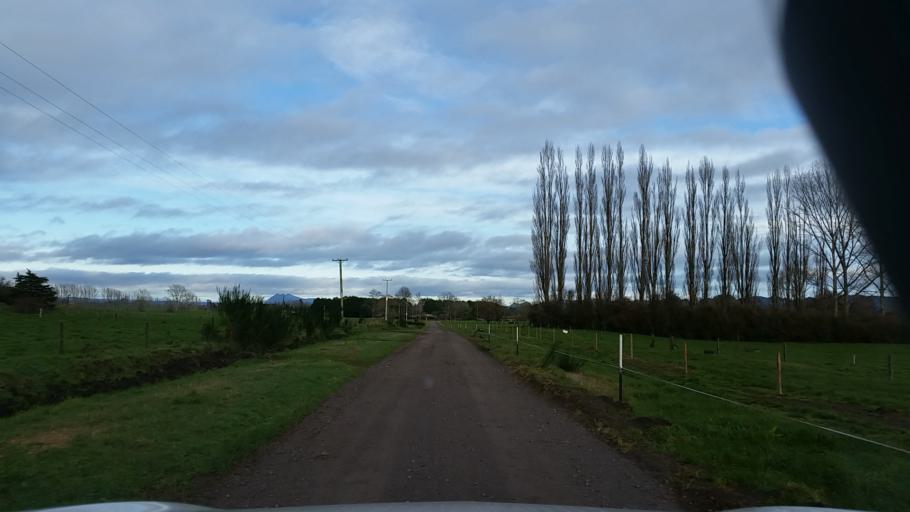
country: NZ
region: Bay of Plenty
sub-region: Rotorua District
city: Rotorua
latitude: -38.3935
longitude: 176.3917
